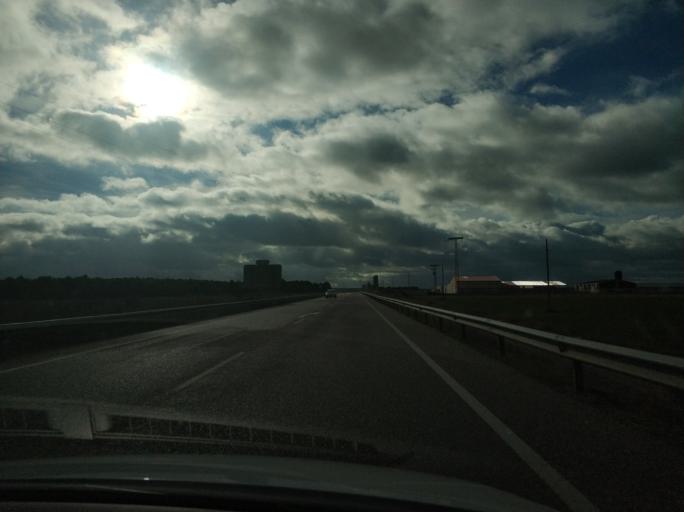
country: ES
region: Castille and Leon
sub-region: Provincia de Segovia
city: Ayllon
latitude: 41.4104
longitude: -3.4129
